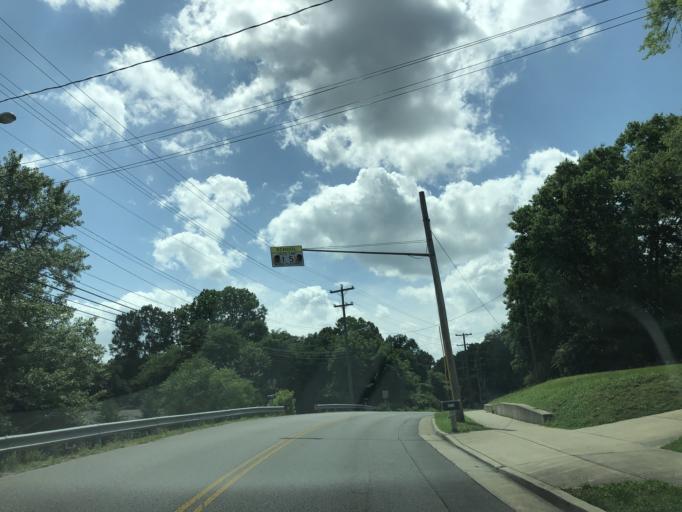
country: US
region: Tennessee
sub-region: Davidson County
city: Oak Hill
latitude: 36.0842
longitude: -86.7350
